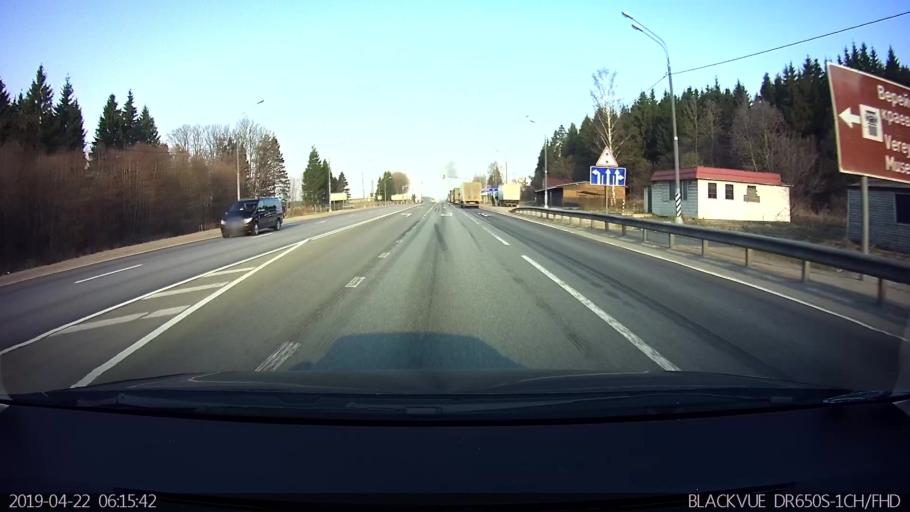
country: RU
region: Moskovskaya
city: Mozhaysk
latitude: 55.4590
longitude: 36.0386
